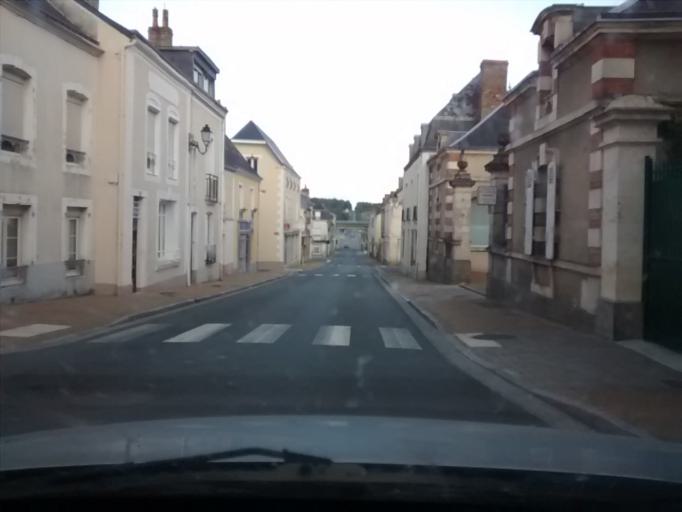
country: FR
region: Pays de la Loire
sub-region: Departement de la Sarthe
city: Sille-le-Guillaume
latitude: 48.1832
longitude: -0.1270
